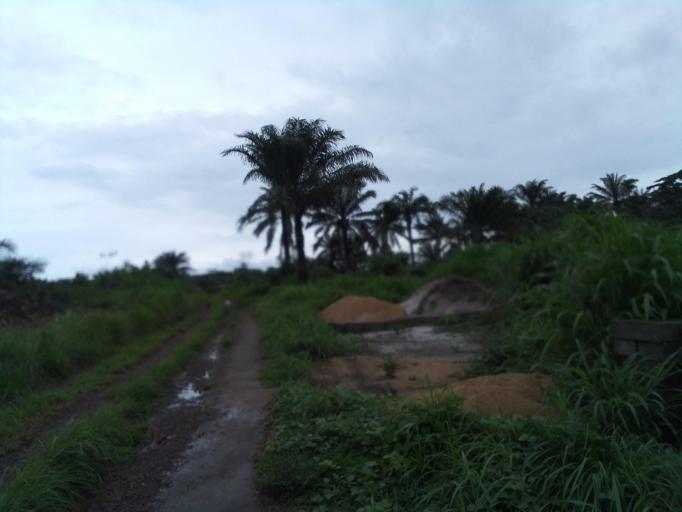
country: SL
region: Eastern Province
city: Kenema
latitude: 7.8747
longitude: -11.1564
